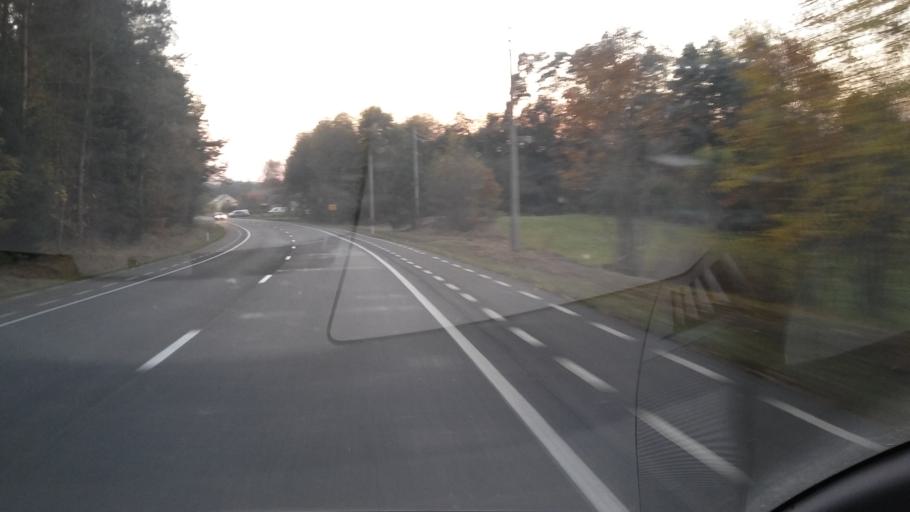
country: BE
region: Wallonia
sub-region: Province du Luxembourg
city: Saint-Leger
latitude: 49.6817
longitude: 5.7097
